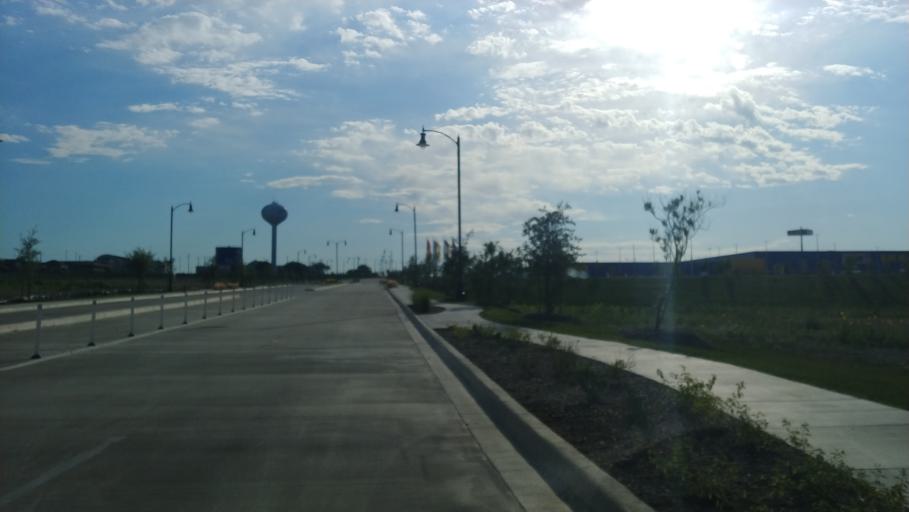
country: US
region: Texas
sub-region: Bexar County
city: Live Oak
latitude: 29.5659
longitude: -98.3426
